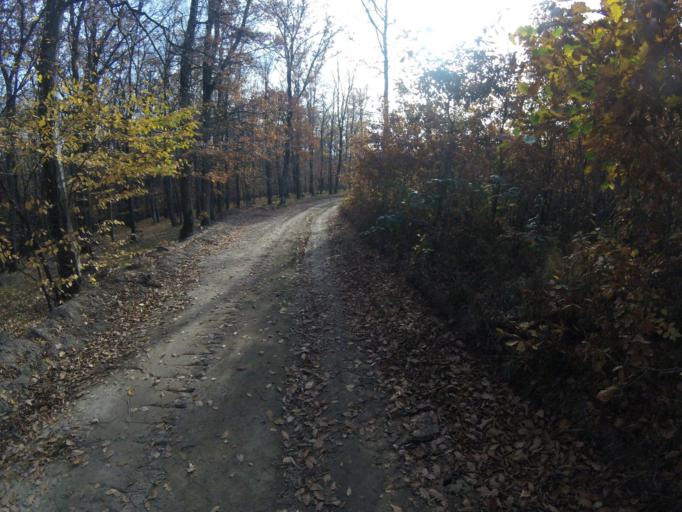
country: HU
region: Borsod-Abauj-Zemplen
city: Satoraljaujhely
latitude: 48.4199
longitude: 21.5785
